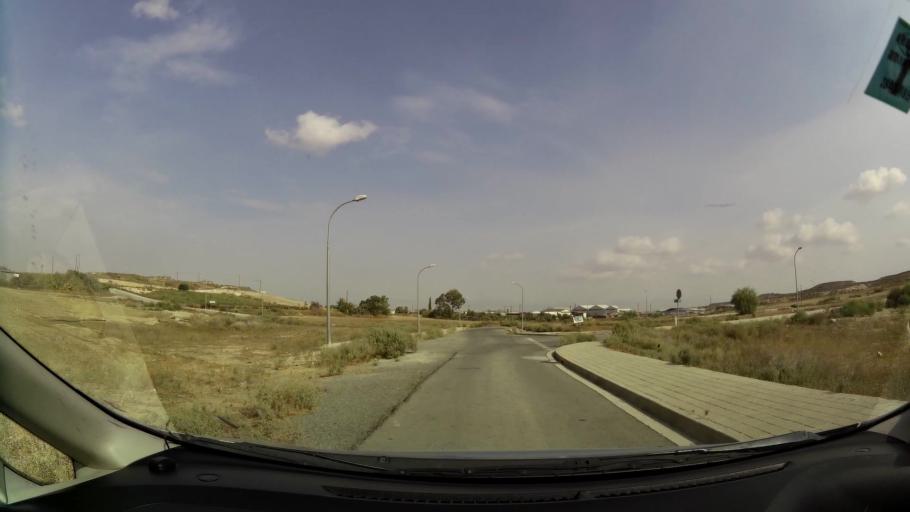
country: CY
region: Lefkosia
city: Geri
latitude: 35.0679
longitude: 33.4025
